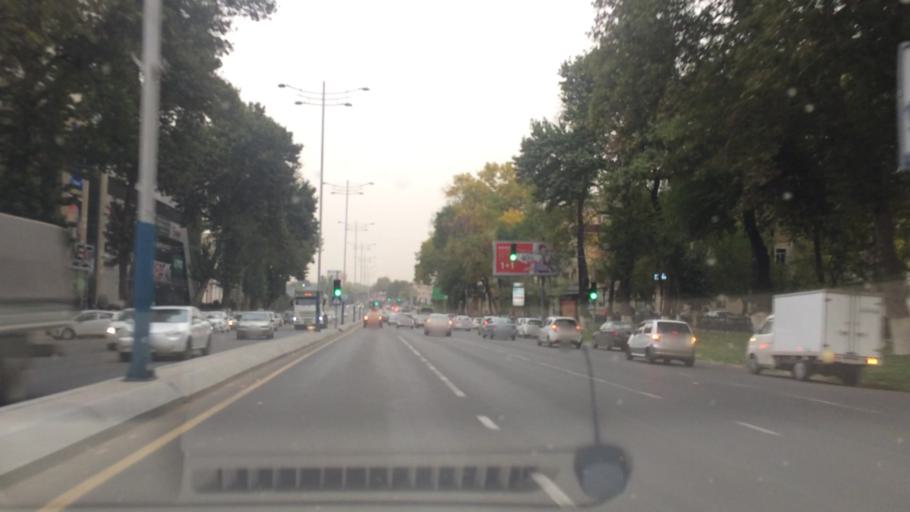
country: UZ
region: Toshkent Shahri
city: Tashkent
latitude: 41.2976
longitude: 69.2501
